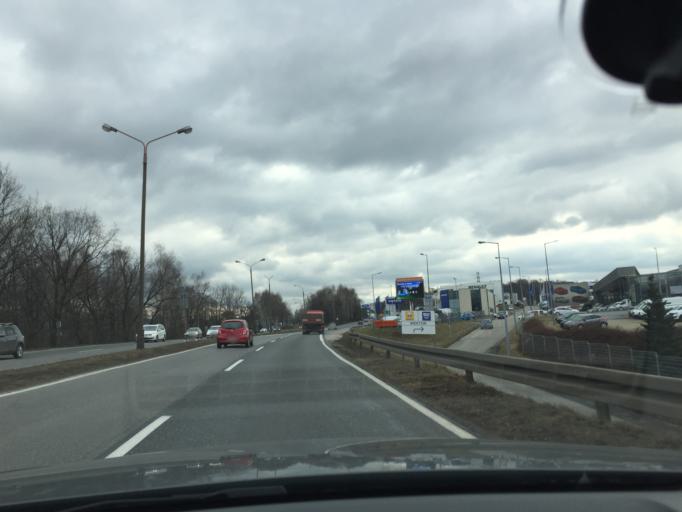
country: PL
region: Silesian Voivodeship
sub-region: Bielsko-Biala
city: Bielsko-Biala
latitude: 49.8564
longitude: 19.0270
